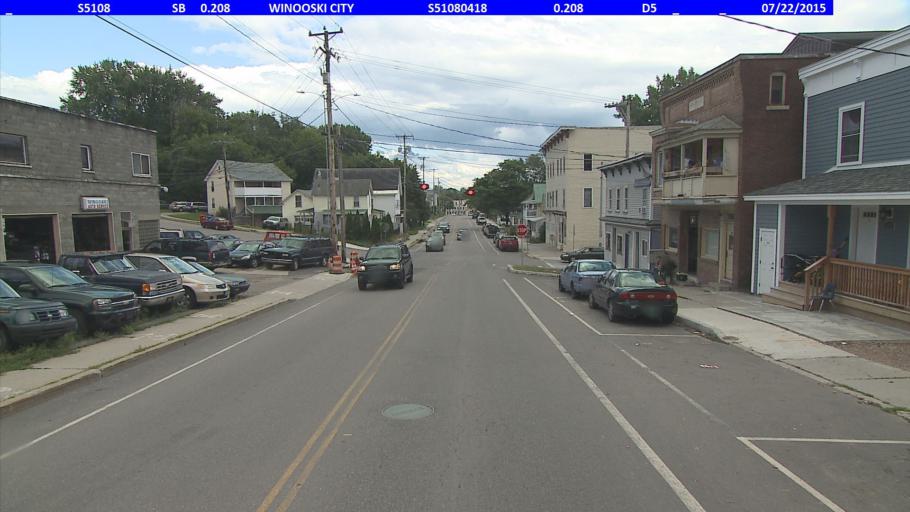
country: US
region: Vermont
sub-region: Chittenden County
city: Winooski
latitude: 44.4939
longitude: -73.1915
